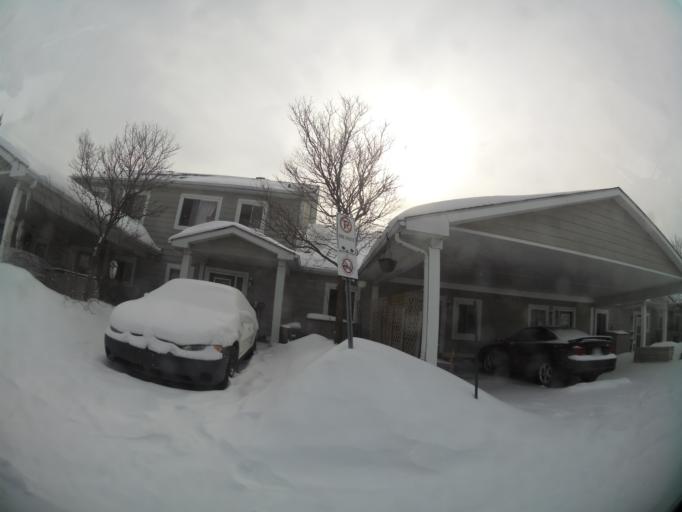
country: CA
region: Ontario
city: Ottawa
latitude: 45.3734
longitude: -75.6001
